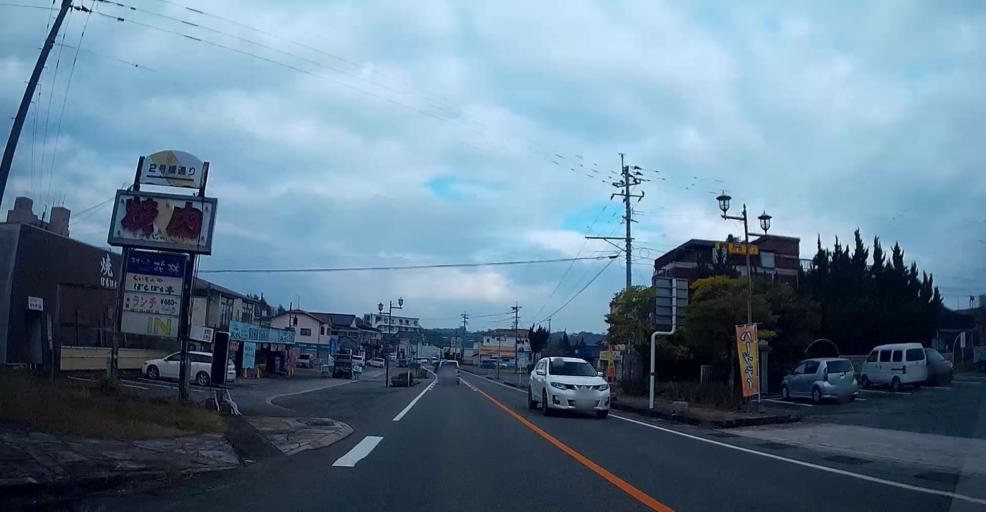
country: JP
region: Kumamoto
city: Yatsushiro
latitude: 32.5481
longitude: 130.4220
